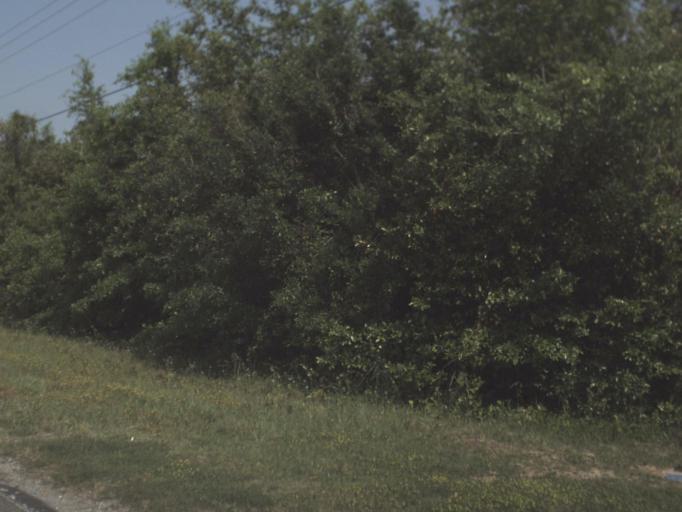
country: US
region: Florida
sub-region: Escambia County
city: Myrtle Grove
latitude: 30.4200
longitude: -87.3521
